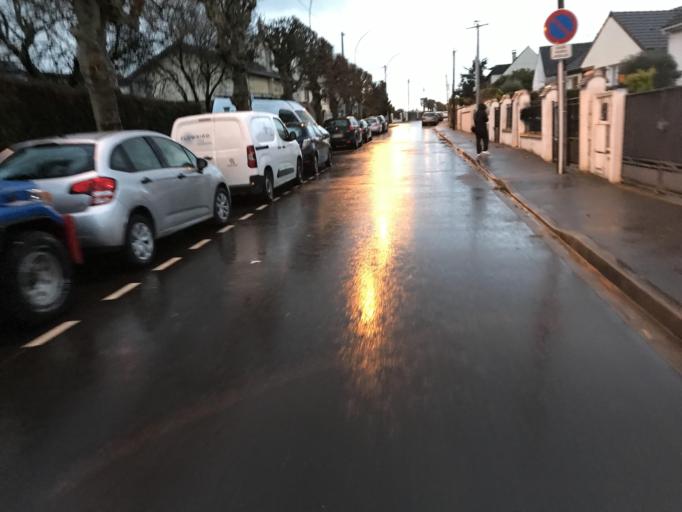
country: FR
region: Ile-de-France
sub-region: Departement de l'Essonne
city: Morangis
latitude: 48.7013
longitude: 2.3505
